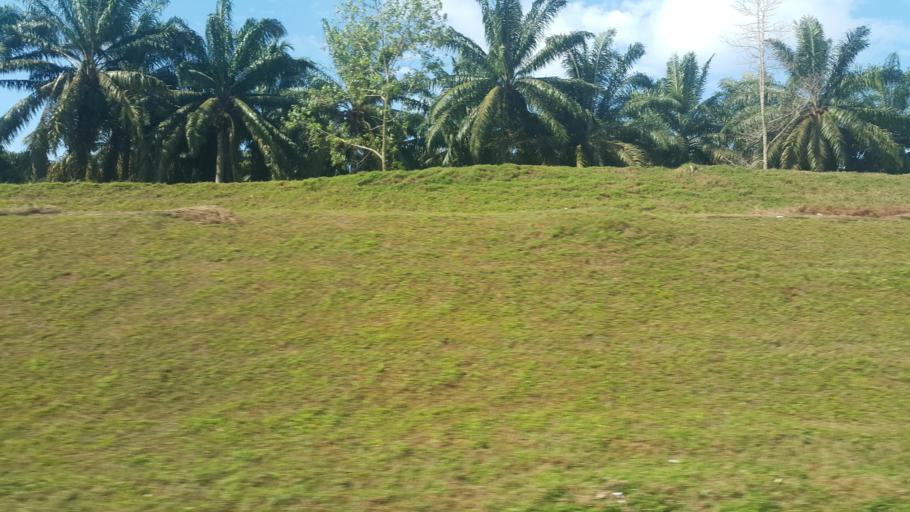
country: MY
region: Johor
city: Kelapa Sawit
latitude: 1.7330
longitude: 103.4174
